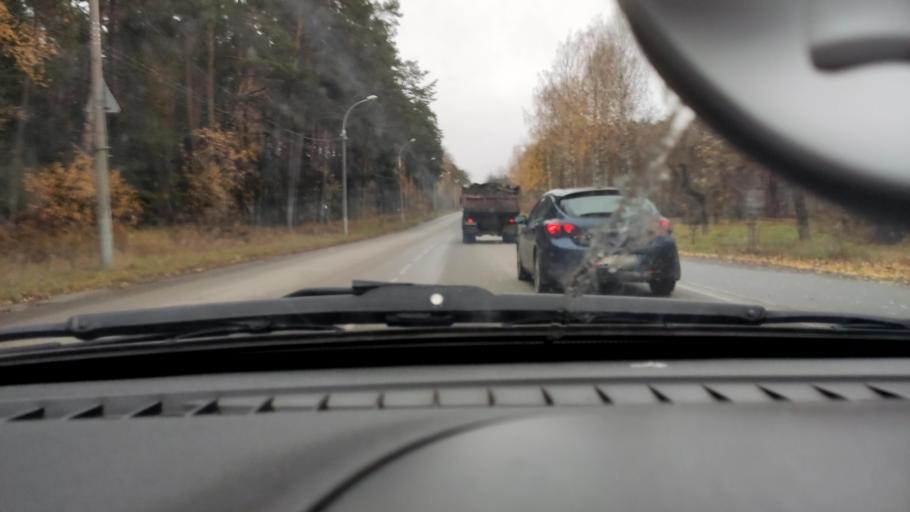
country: RU
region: Perm
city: Kondratovo
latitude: 58.0168
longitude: 55.9981
